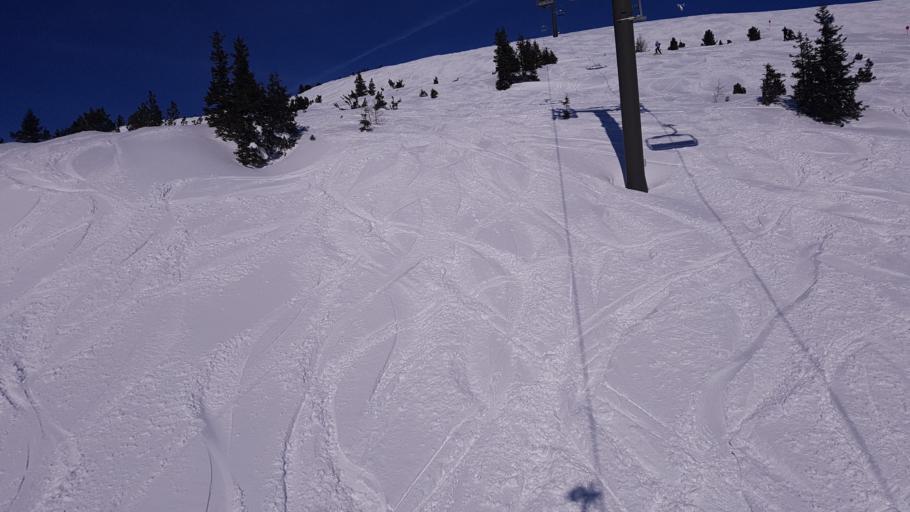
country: AT
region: Salzburg
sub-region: Politischer Bezirk Zell am See
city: Neukirchen am Grossvenediger
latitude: 47.2785
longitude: 12.2656
